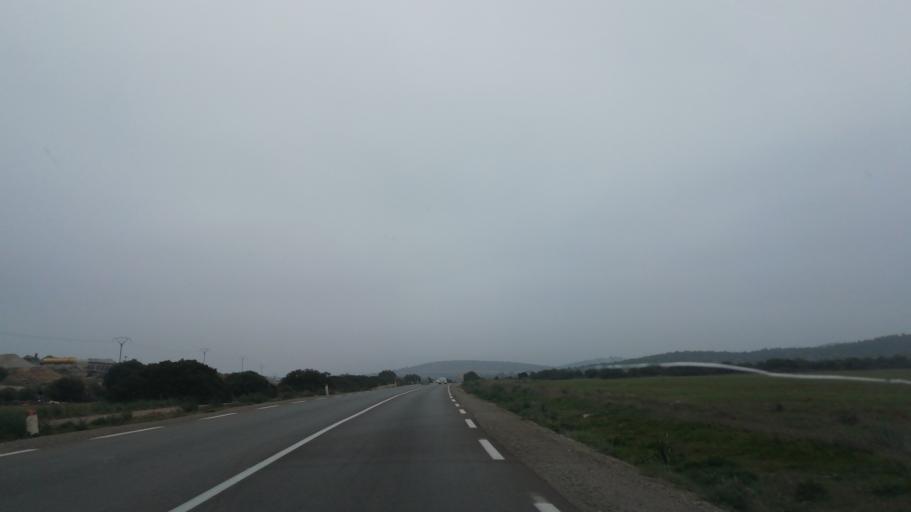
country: DZ
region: Mascara
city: Oued el Abtal
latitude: 35.3016
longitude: 0.4427
